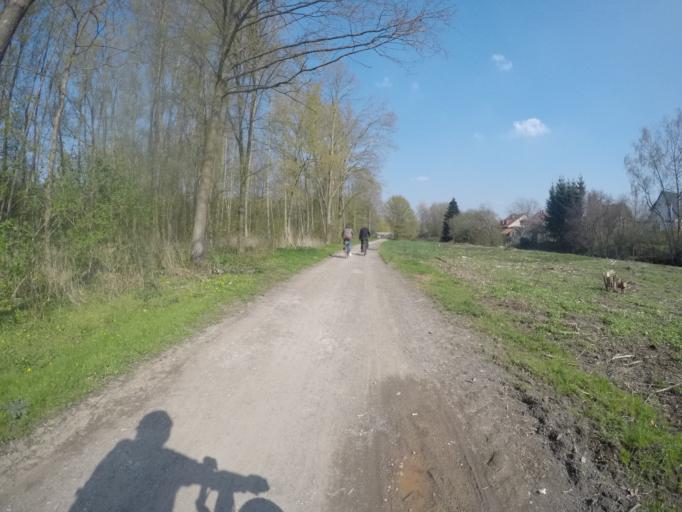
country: DE
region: North Rhine-Westphalia
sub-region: Regierungsbezirk Detmold
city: Bielefeld
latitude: 52.0378
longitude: 8.6100
